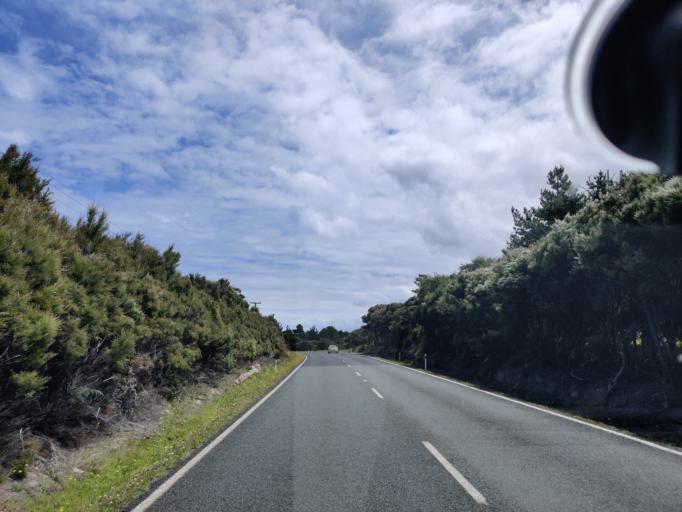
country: NZ
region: Northland
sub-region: Far North District
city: Kaitaia
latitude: -34.6649
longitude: 172.9729
